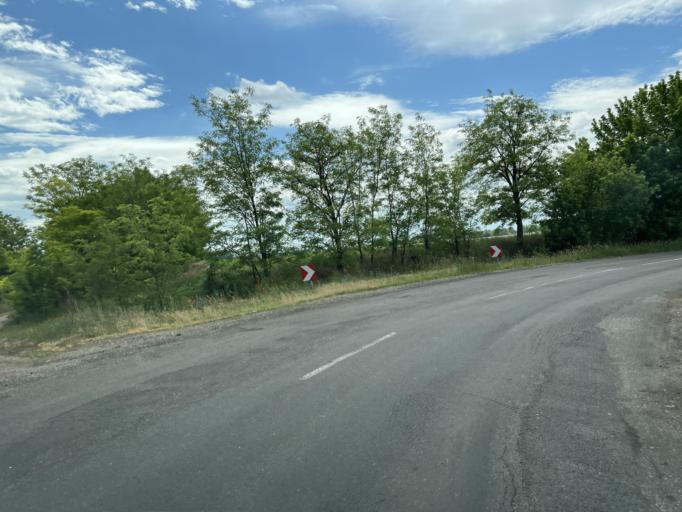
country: HU
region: Pest
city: Szentlorinckata
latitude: 47.4930
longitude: 19.7384
